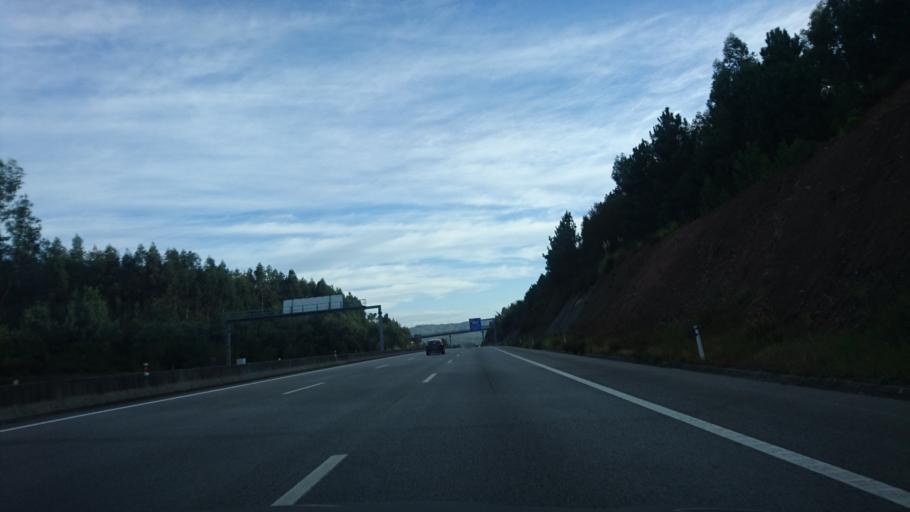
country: PT
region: Porto
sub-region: Vila Nova de Gaia
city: Sandim
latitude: 41.0517
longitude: -8.4738
